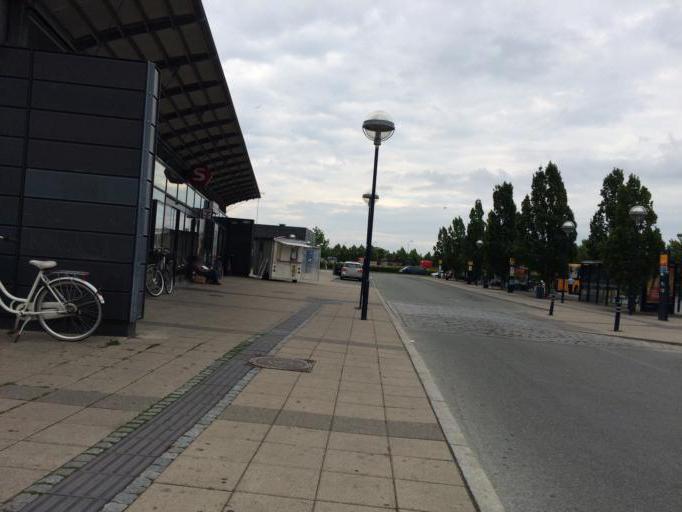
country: DK
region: Capital Region
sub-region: Hvidovre Kommune
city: Hvidovre
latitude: 55.6288
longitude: 12.4821
